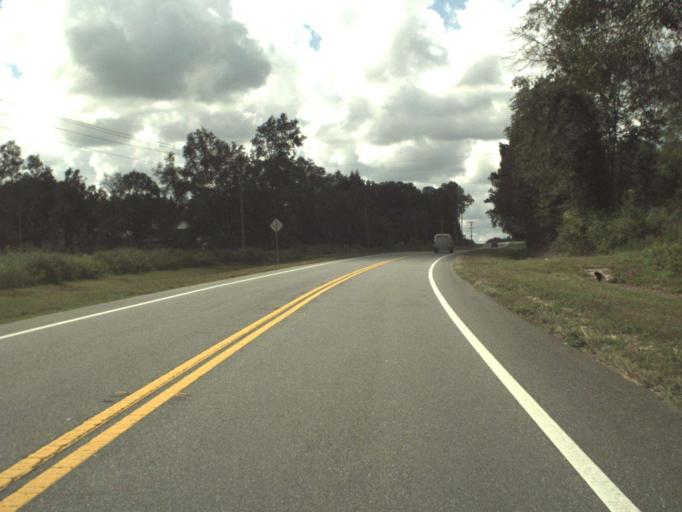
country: US
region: Florida
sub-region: Washington County
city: Chipley
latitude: 30.8178
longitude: -85.5054
